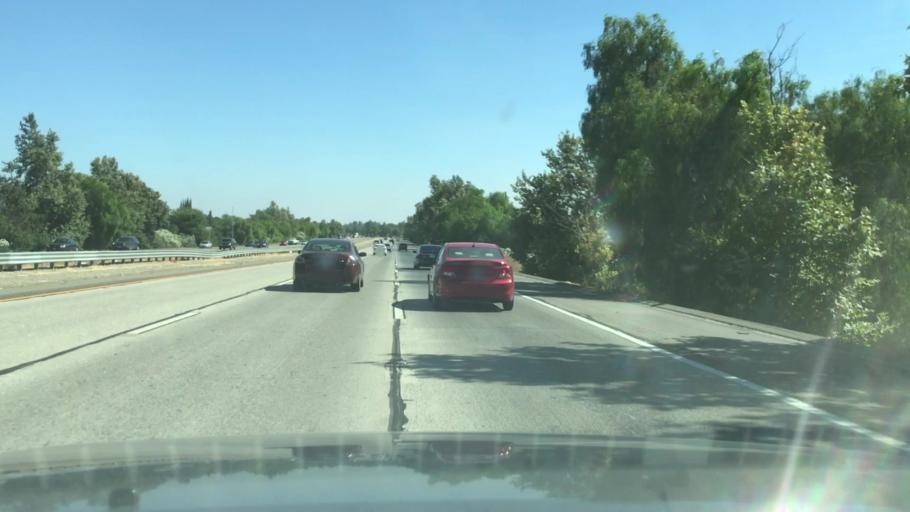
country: US
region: California
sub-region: San Joaquin County
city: Lincoln Village
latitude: 38.0411
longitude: -121.3682
